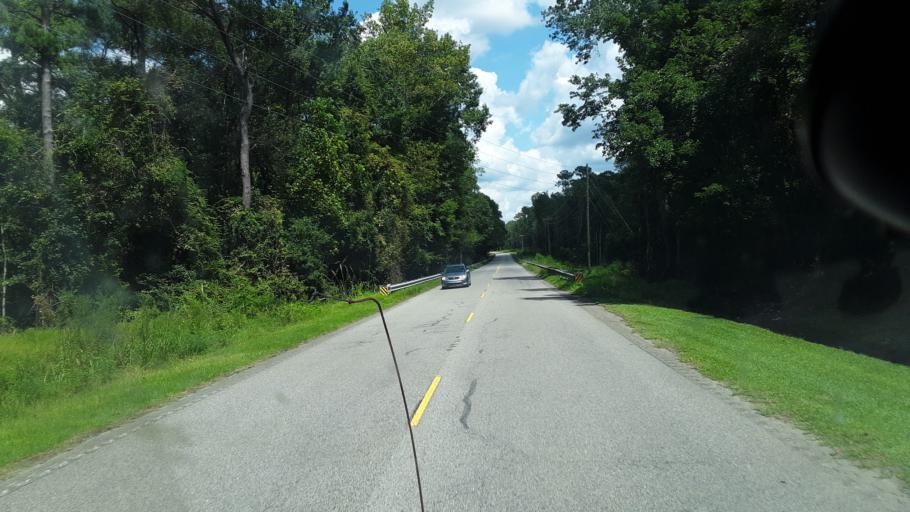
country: US
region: South Carolina
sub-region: Williamsburg County
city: Andrews
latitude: 33.5145
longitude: -79.5017
